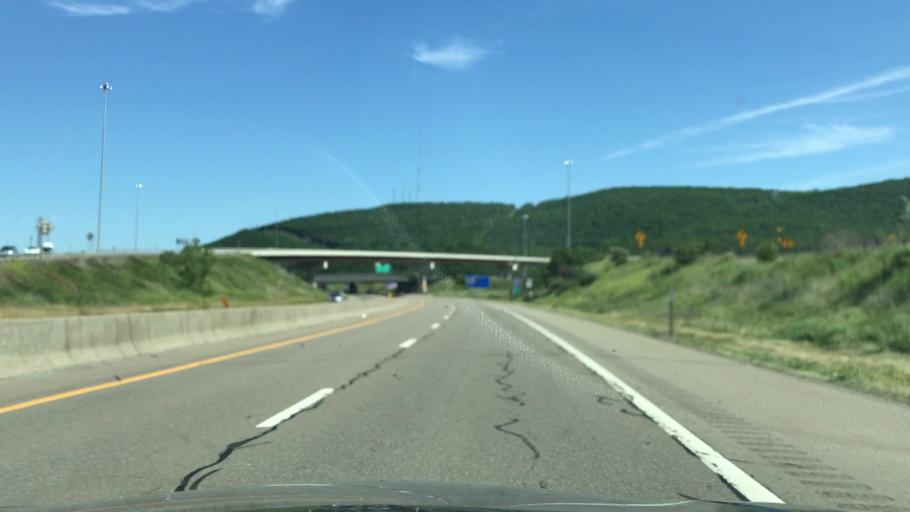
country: US
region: New York
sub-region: Steuben County
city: Painted Post
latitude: 42.1588
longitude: -77.0994
